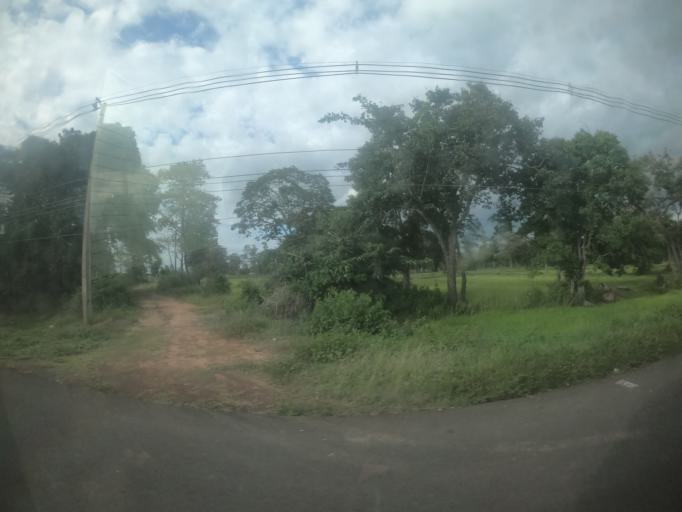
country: TH
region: Surin
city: Prasat
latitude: 14.5738
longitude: 103.4846
